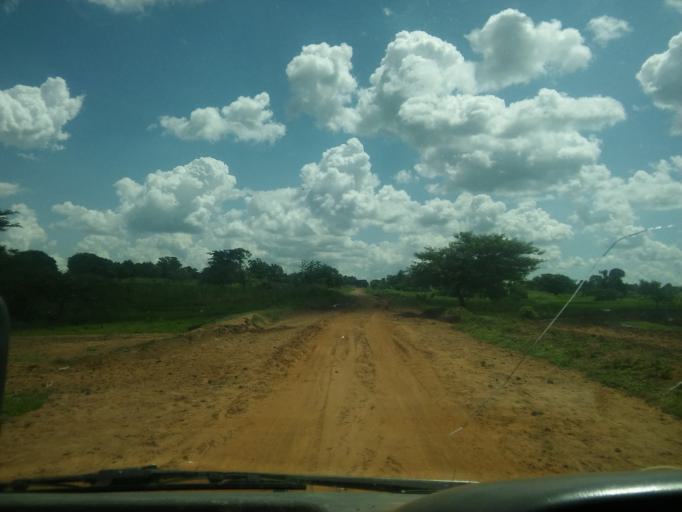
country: UG
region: Eastern Region
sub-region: Pallisa District
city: Pallisa
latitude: 1.1501
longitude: 33.8180
